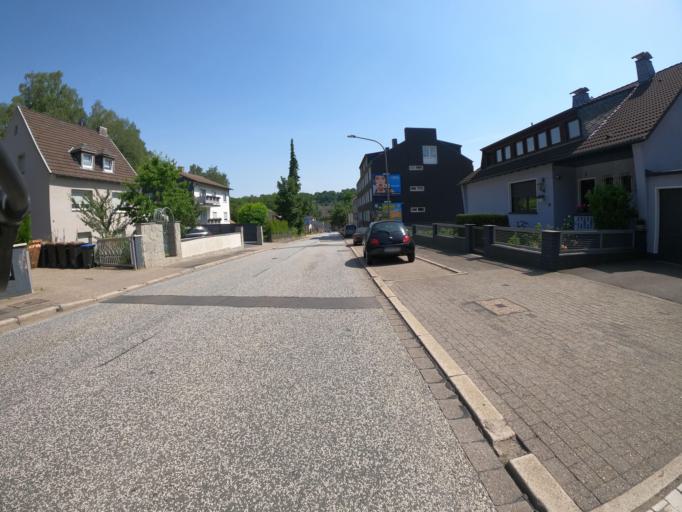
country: DE
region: North Rhine-Westphalia
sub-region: Regierungsbezirk Dusseldorf
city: Wuppertal
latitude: 51.2692
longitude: 7.1593
